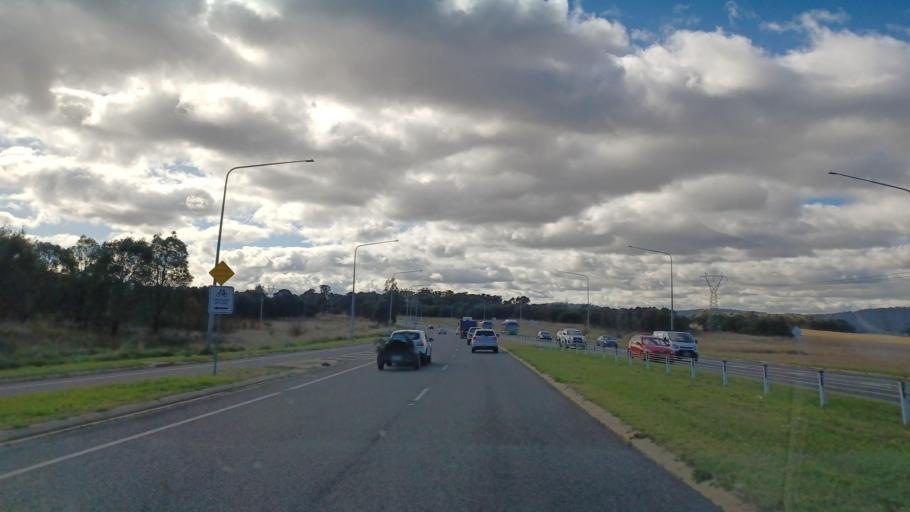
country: AU
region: Australian Capital Territory
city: Kaleen
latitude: -35.2245
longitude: 149.1247
